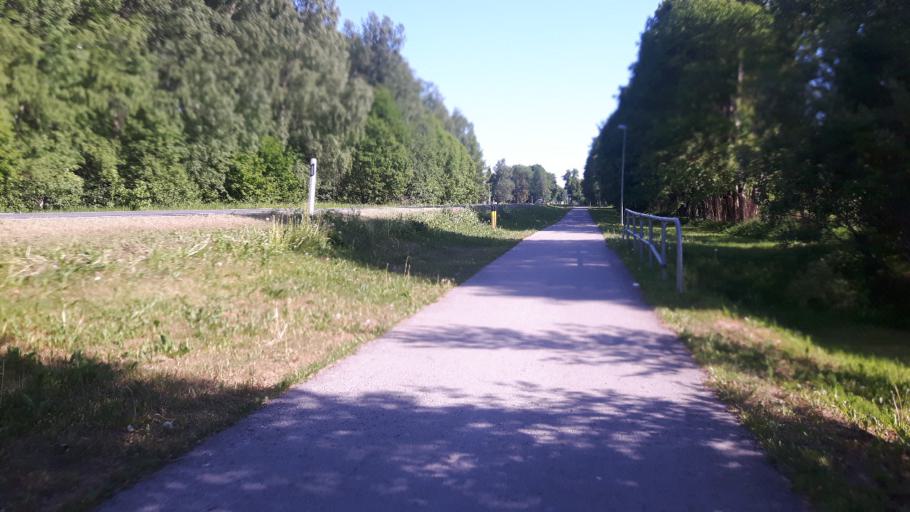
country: EE
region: Raplamaa
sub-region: Rapla vald
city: Rapla
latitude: 58.9823
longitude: 24.8438
